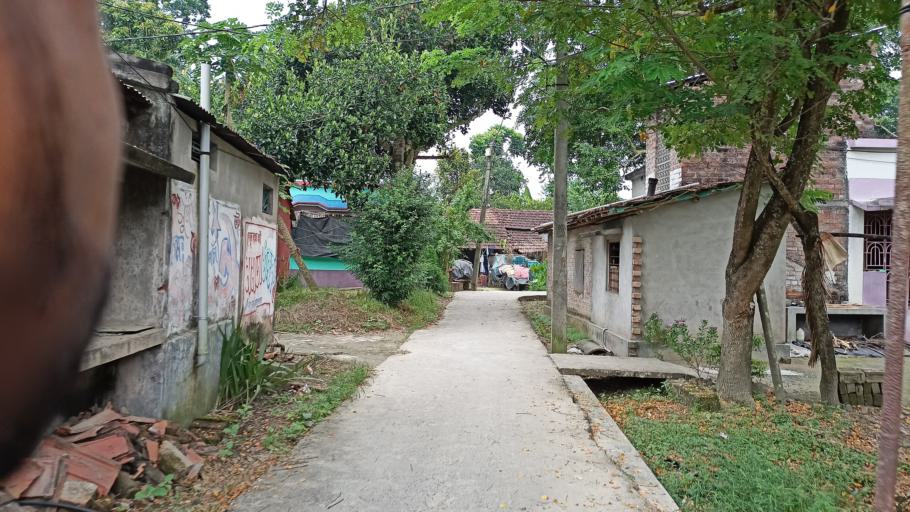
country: IN
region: West Bengal
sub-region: North 24 Parganas
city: Bangaon
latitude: 23.0653
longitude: 88.8196
